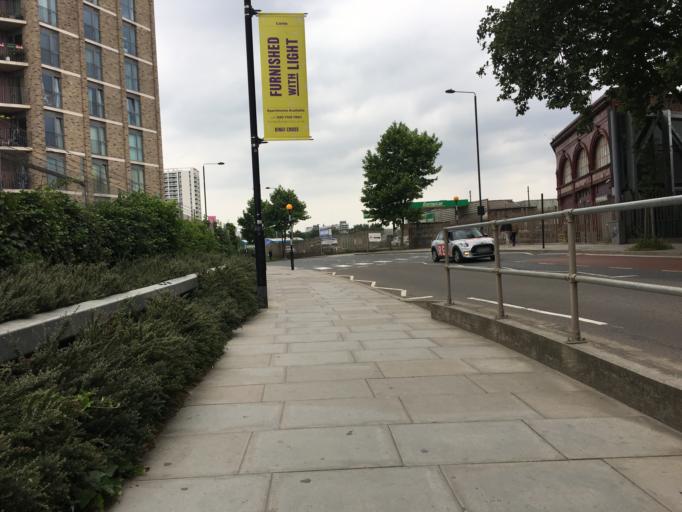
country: GB
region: England
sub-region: Greater London
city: Barnsbury
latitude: 51.5379
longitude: -0.1228
